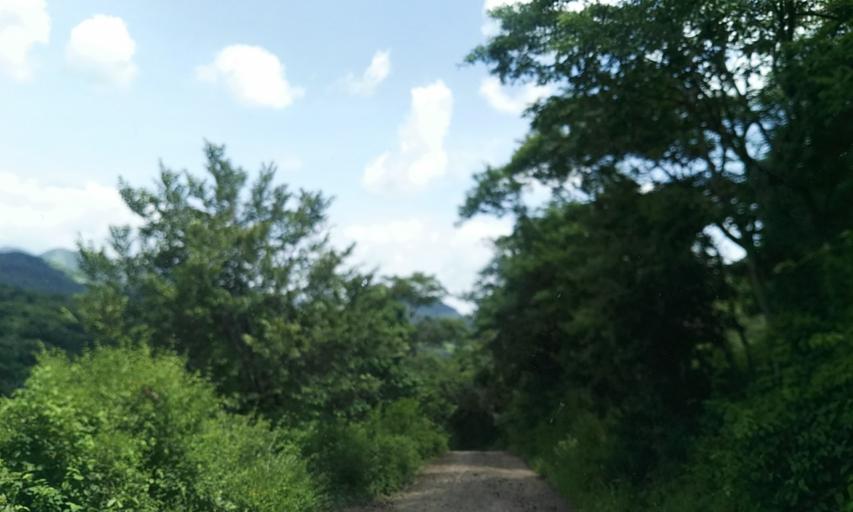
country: NI
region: Matagalpa
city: Terrabona
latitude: 12.7268
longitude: -85.9289
